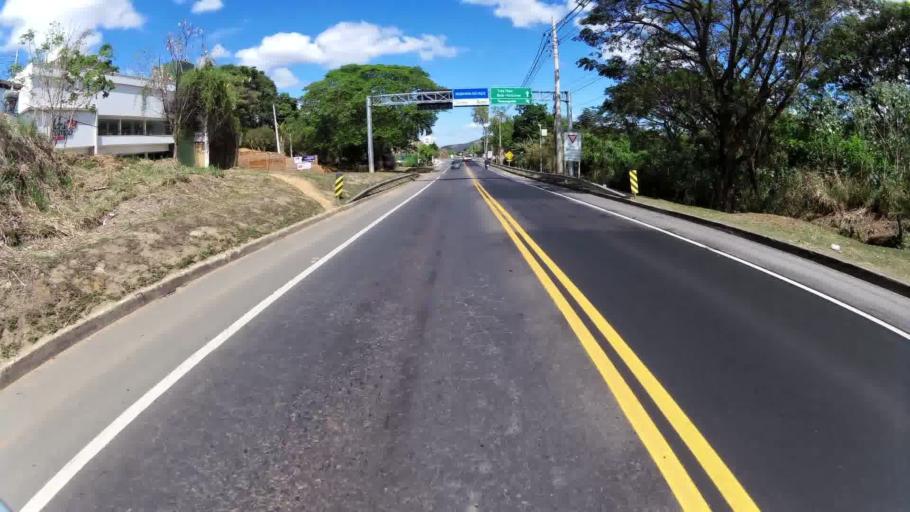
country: BR
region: Minas Gerais
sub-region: Alem Paraiba
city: Alem Paraiba
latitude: -21.8790
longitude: -42.6793
